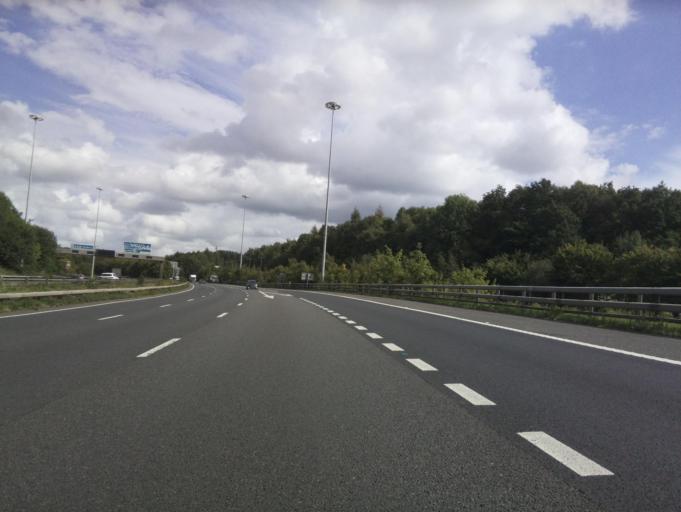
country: GB
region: England
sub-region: Borough of Stockport
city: Bredbury
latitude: 53.4211
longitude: -2.1306
